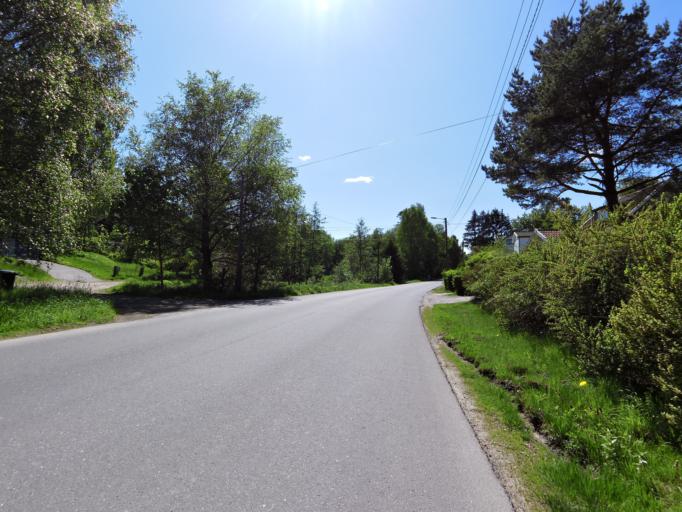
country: NO
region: Ostfold
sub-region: Fredrikstad
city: Fredrikstad
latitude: 59.2254
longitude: 10.9661
